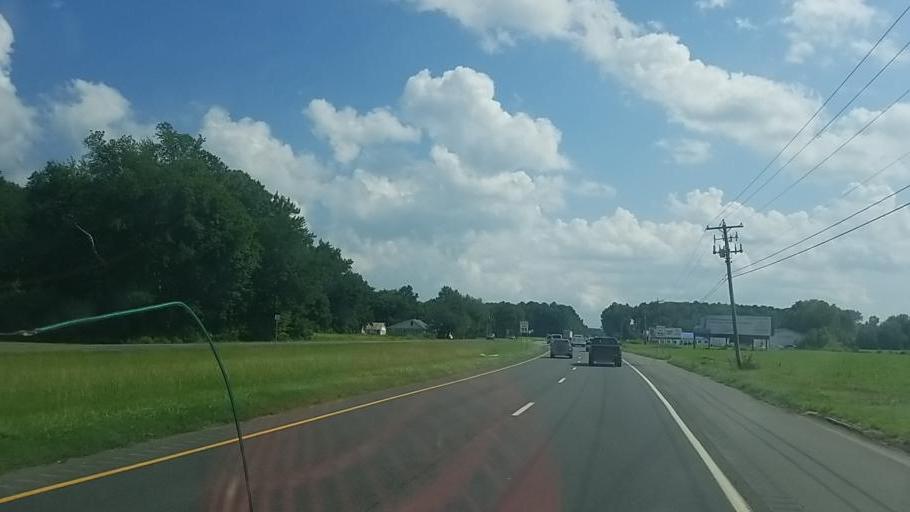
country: US
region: Delaware
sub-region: Sussex County
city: Selbyville
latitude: 38.5114
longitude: -75.2385
